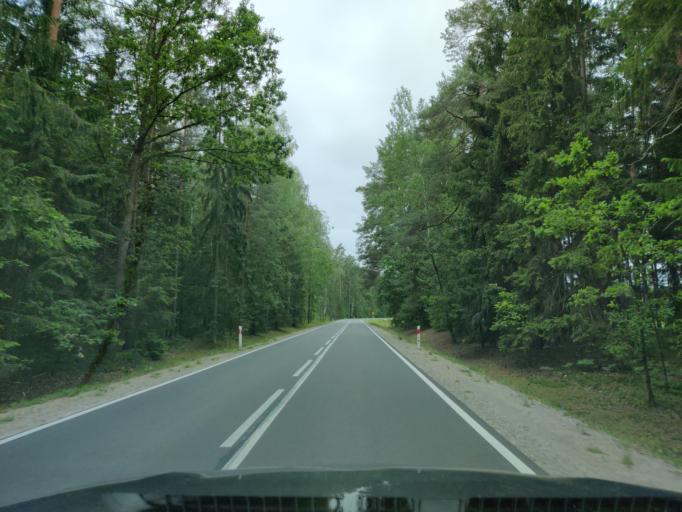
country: PL
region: Masovian Voivodeship
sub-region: Powiat ostrolecki
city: Czarnia
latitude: 53.3288
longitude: 21.1863
